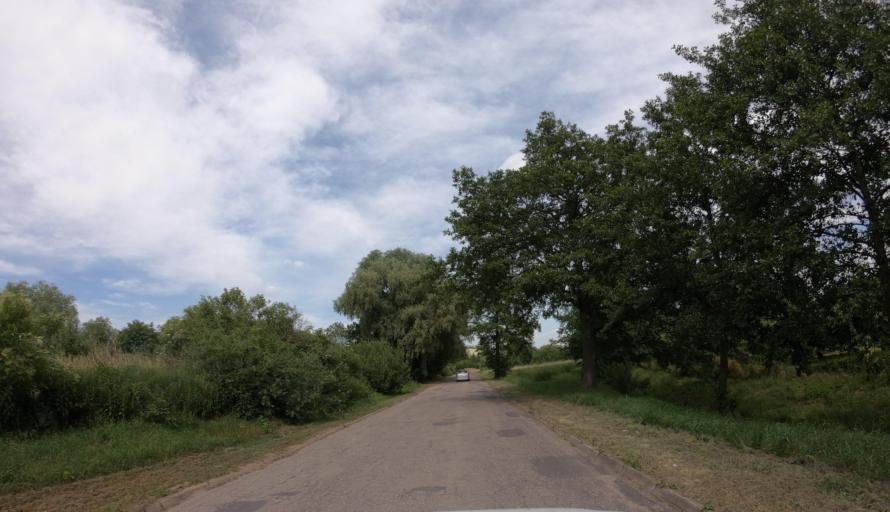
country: PL
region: West Pomeranian Voivodeship
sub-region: Powiat pyrzycki
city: Pyrzyce
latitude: 53.1415
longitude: 14.8735
